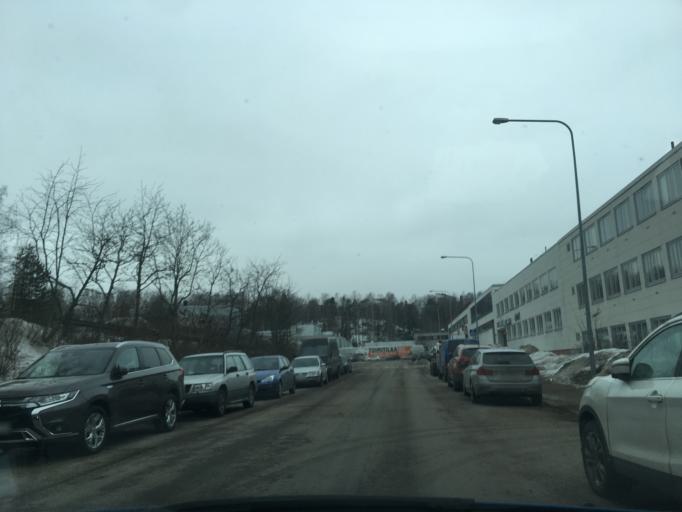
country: FI
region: Uusimaa
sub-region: Helsinki
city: Vantaa
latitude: 60.2103
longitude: 25.0503
